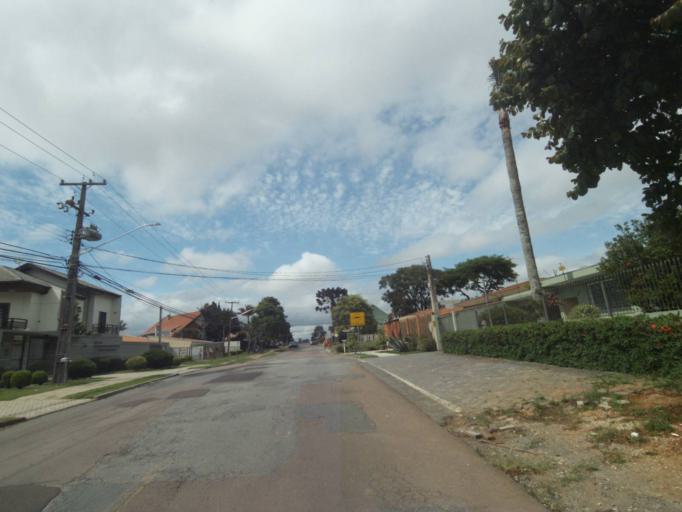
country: BR
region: Parana
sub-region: Pinhais
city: Pinhais
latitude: -25.4310
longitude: -49.2277
